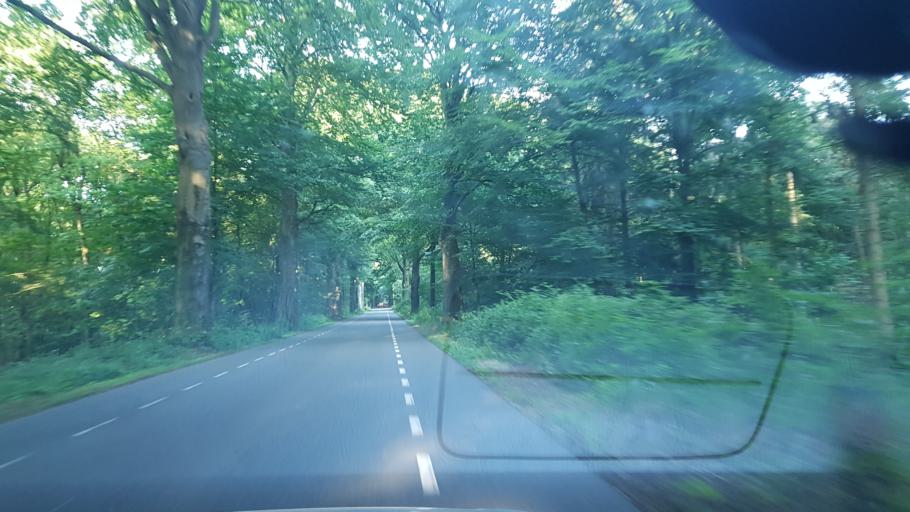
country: NL
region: Gelderland
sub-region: Gemeente Groesbeek
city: Groesbeek
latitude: 51.7743
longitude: 5.9042
